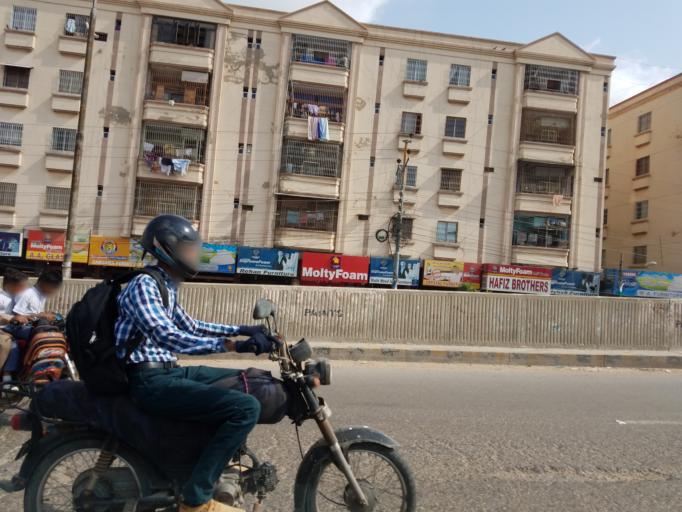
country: PK
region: Sindh
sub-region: Karachi District
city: Karachi
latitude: 24.9202
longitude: 67.0552
